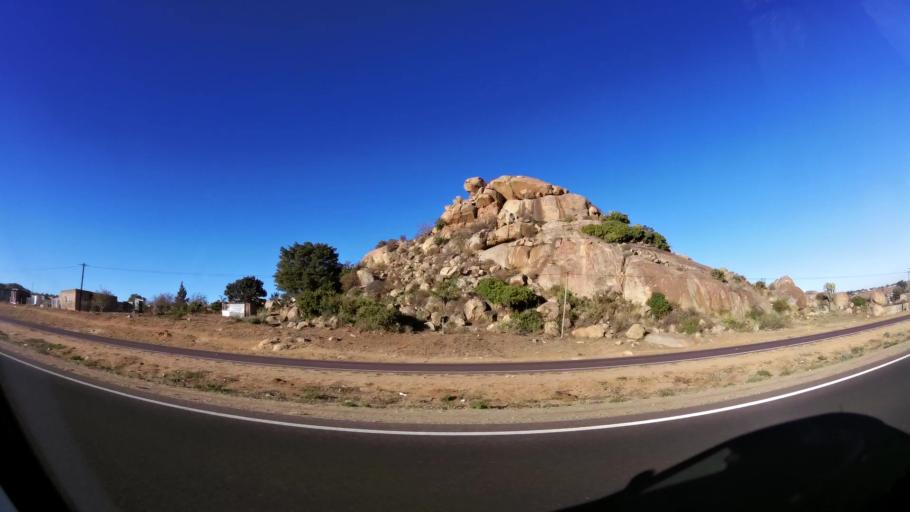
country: ZA
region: Limpopo
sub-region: Capricorn District Municipality
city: Mankoeng
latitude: -23.9058
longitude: 29.7602
